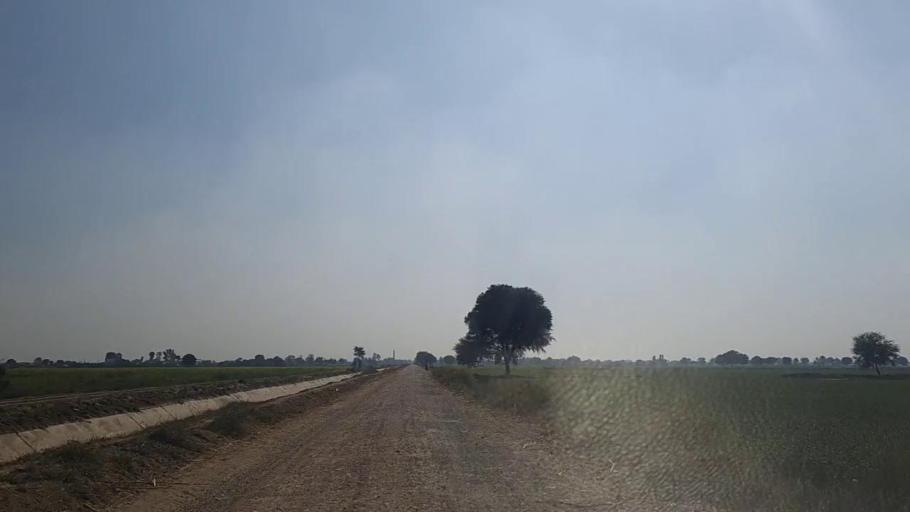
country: PK
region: Sindh
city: Shahpur Chakar
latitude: 26.1999
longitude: 68.5837
